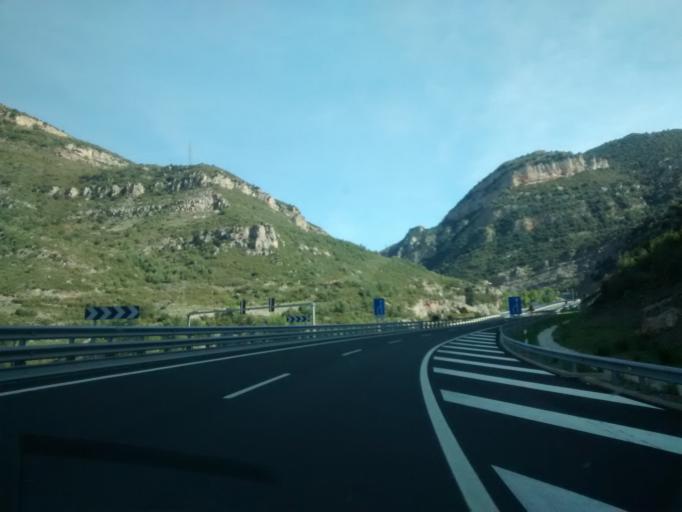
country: ES
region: Aragon
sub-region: Provincia de Huesca
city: Nueno
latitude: 42.2842
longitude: -0.4248
